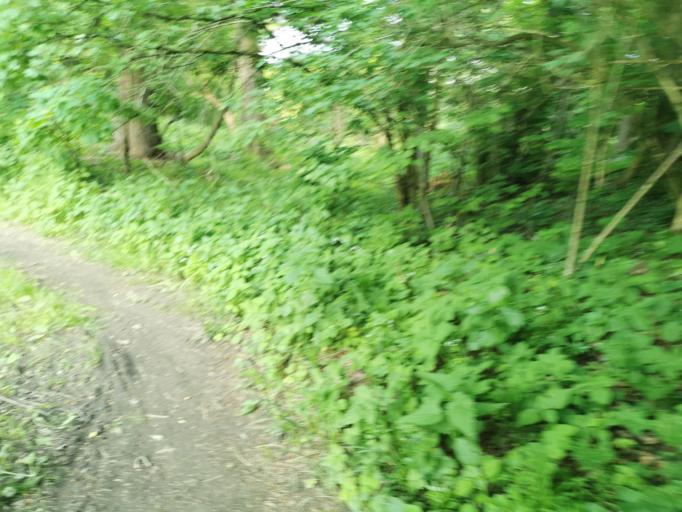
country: CZ
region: South Moravian
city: Knezdub
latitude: 48.8673
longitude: 17.4103
